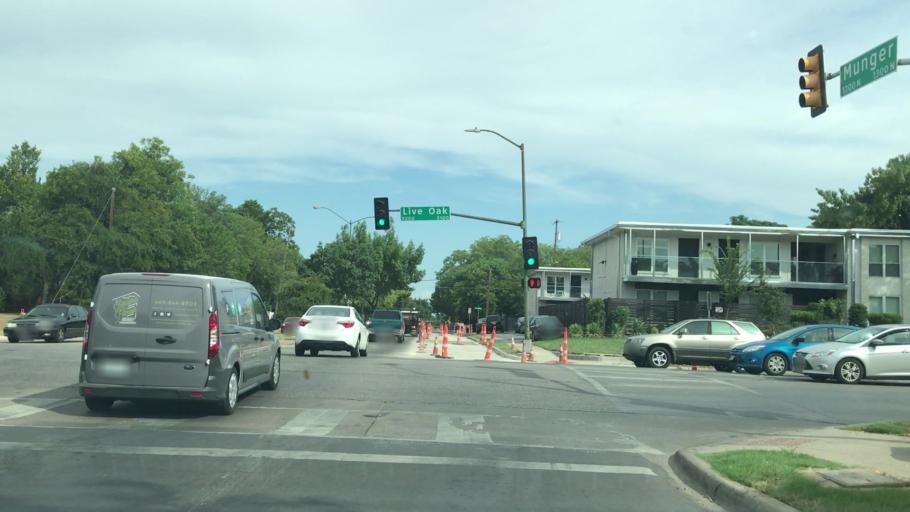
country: US
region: Texas
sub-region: Dallas County
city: Highland Park
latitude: 32.8056
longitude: -96.7692
